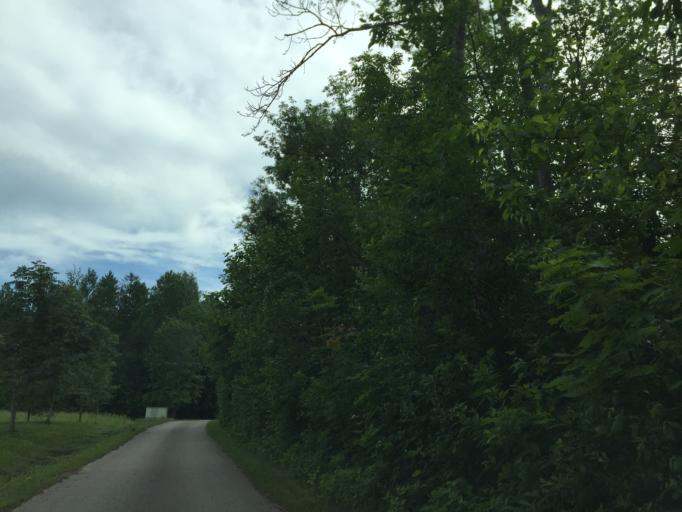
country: LV
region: Engure
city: Smarde
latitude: 57.0262
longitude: 23.2532
